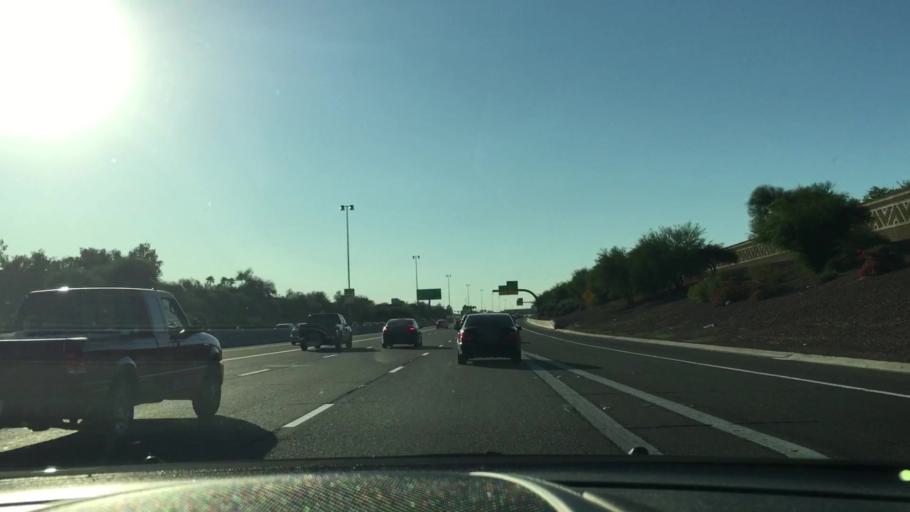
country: US
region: Arizona
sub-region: Maricopa County
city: Peoria
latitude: 33.6681
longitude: -112.2093
